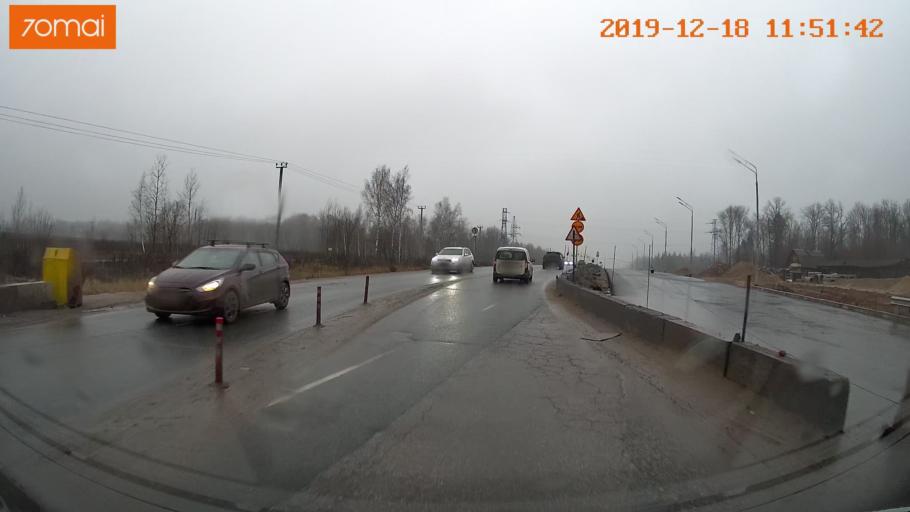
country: RU
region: Moskovskaya
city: Yershovo
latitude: 55.7950
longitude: 36.9215
